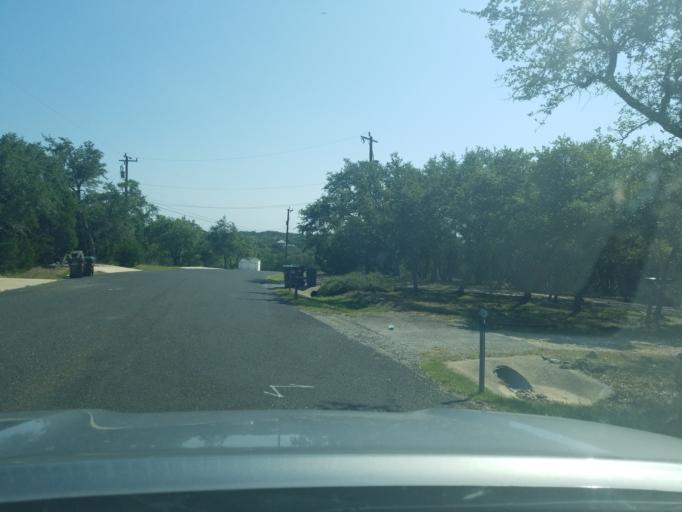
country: US
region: Texas
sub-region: Bexar County
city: Timberwood Park
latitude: 29.6759
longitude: -98.5129
